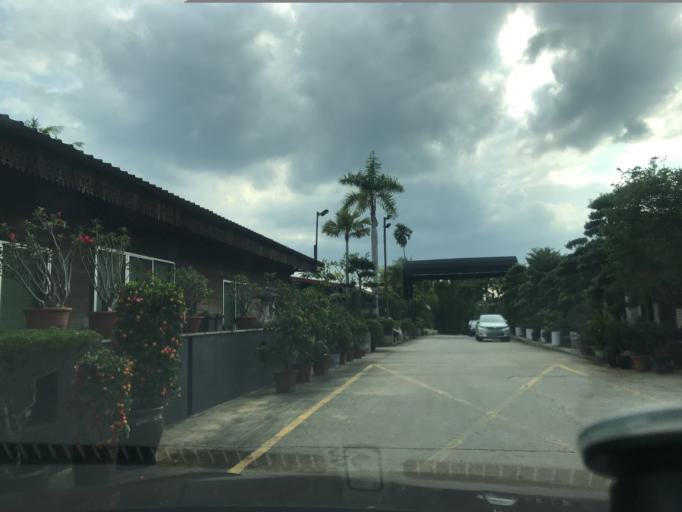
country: MY
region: Johor
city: Johor Bahru
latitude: 1.4410
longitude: 103.7294
